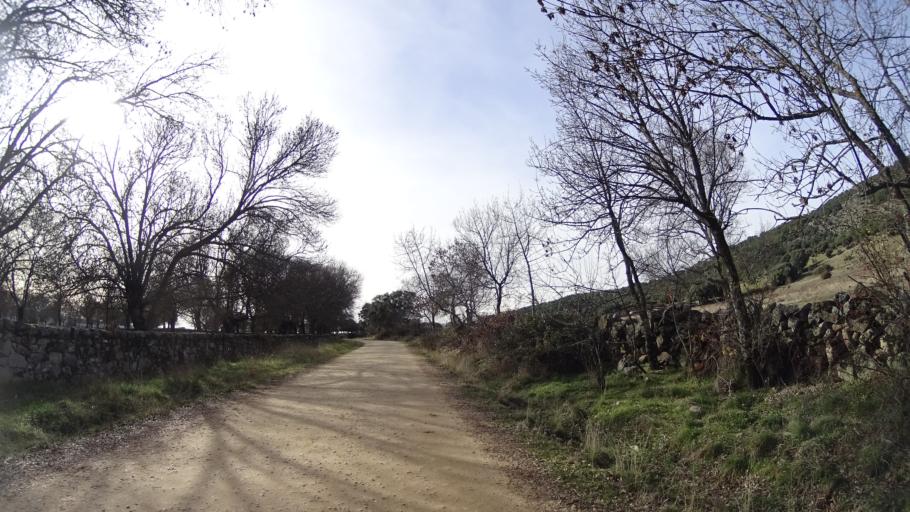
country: ES
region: Madrid
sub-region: Provincia de Madrid
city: Moralzarzal
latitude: 40.6700
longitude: -3.9825
